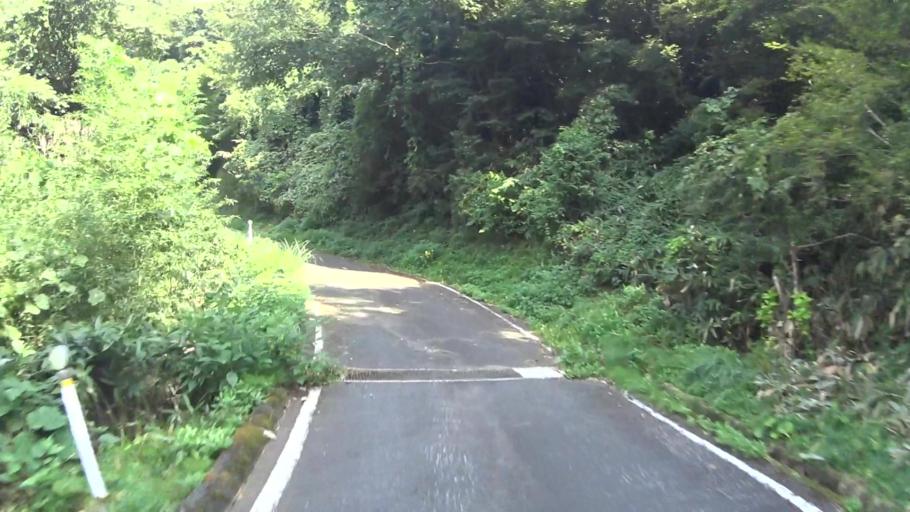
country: JP
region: Kyoto
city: Miyazu
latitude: 35.6568
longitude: 135.2372
